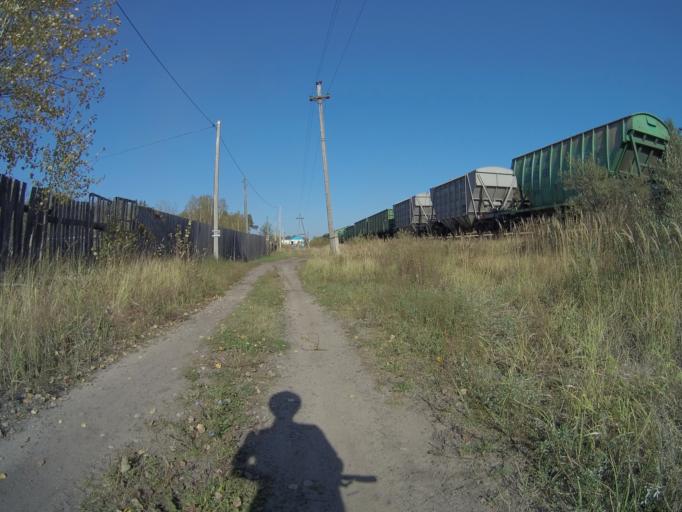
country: RU
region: Vladimir
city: Raduzhnyy
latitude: 56.0256
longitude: 40.3851
